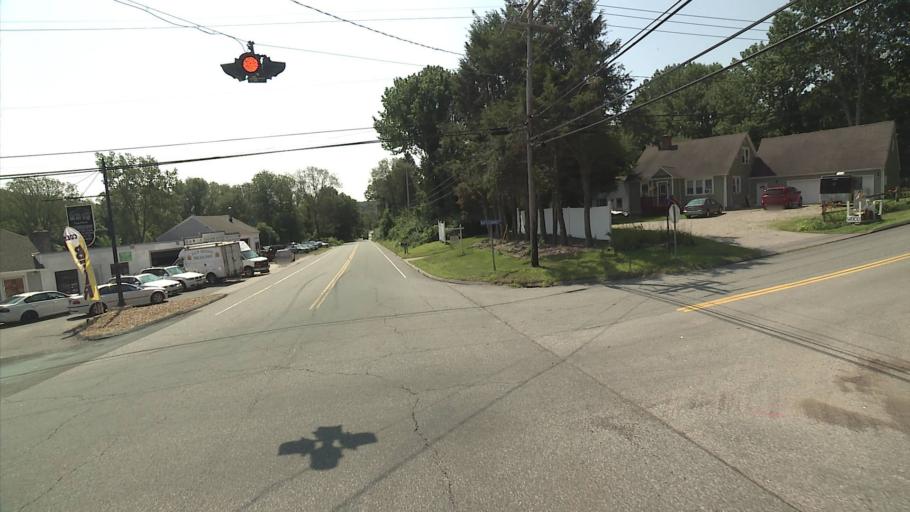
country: US
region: Connecticut
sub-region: New London County
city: Colchester
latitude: 41.5128
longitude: -72.2504
